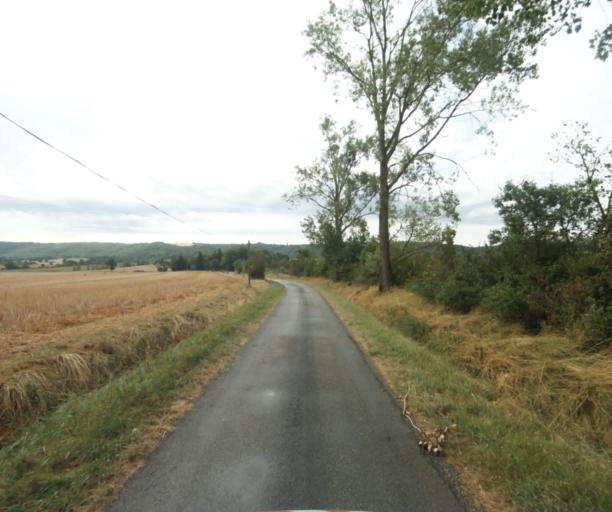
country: FR
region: Midi-Pyrenees
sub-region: Departement de la Haute-Garonne
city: Revel
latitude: 43.4221
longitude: 1.9641
